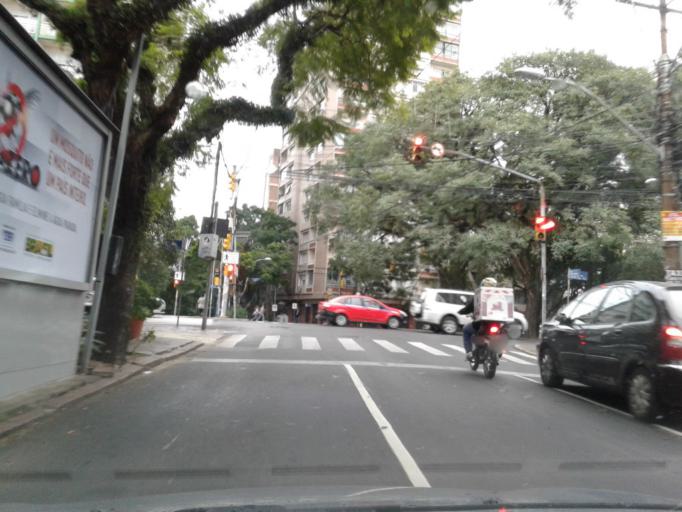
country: BR
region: Rio Grande do Sul
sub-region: Porto Alegre
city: Porto Alegre
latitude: -30.0293
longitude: -51.2085
